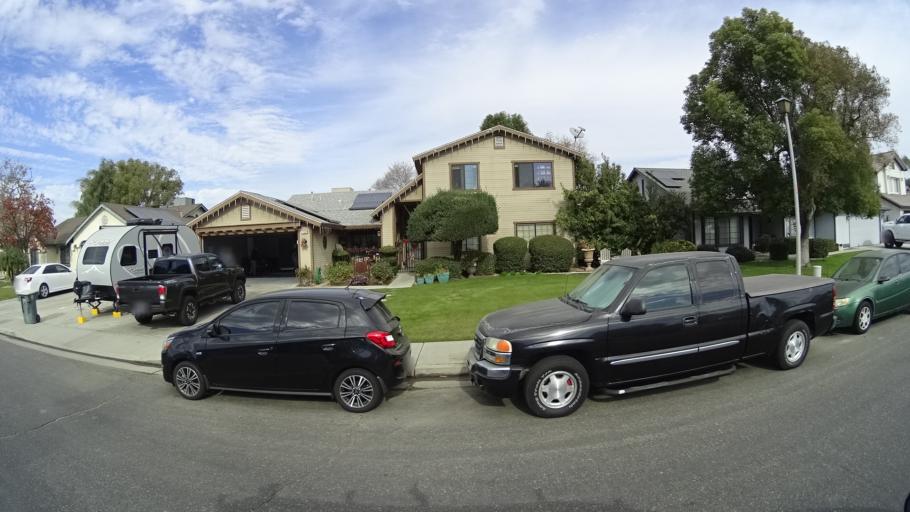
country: US
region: California
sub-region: Kern County
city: Rosedale
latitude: 35.3951
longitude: -119.1309
